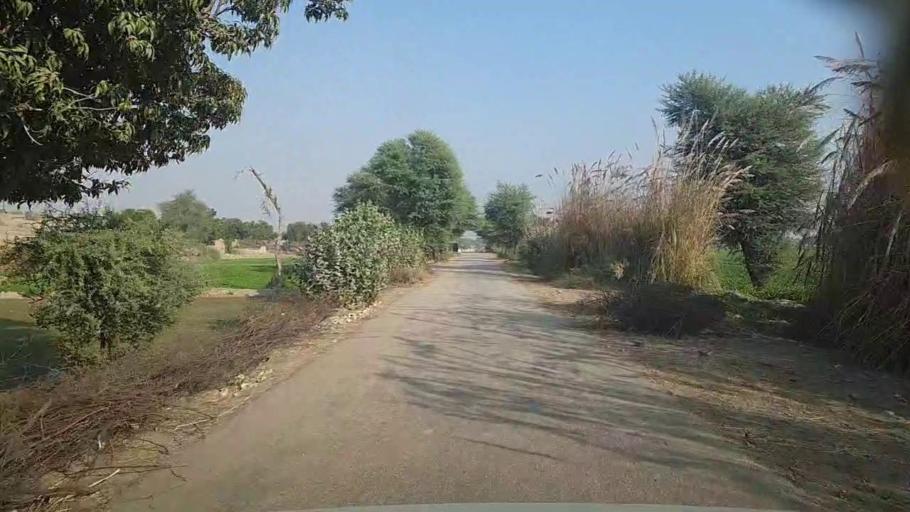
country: PK
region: Sindh
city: Karaundi
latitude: 26.7661
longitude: 68.4853
